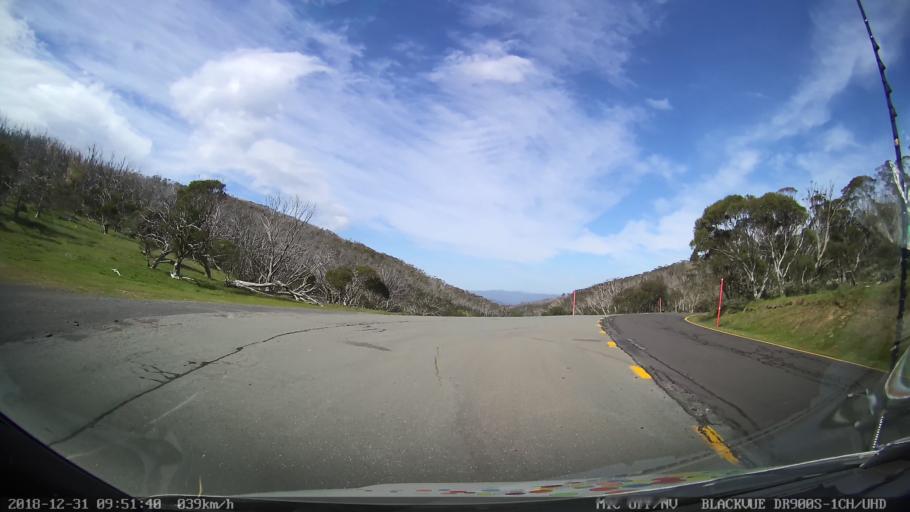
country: AU
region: New South Wales
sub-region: Snowy River
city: Jindabyne
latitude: -36.5241
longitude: 148.2602
